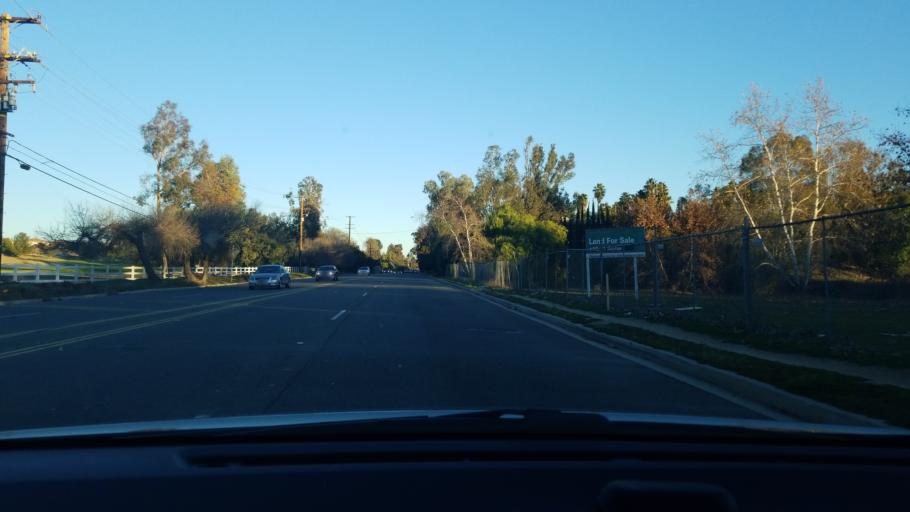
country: US
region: California
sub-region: Riverside County
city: Murrieta Hot Springs
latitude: 33.5561
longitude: -117.1521
